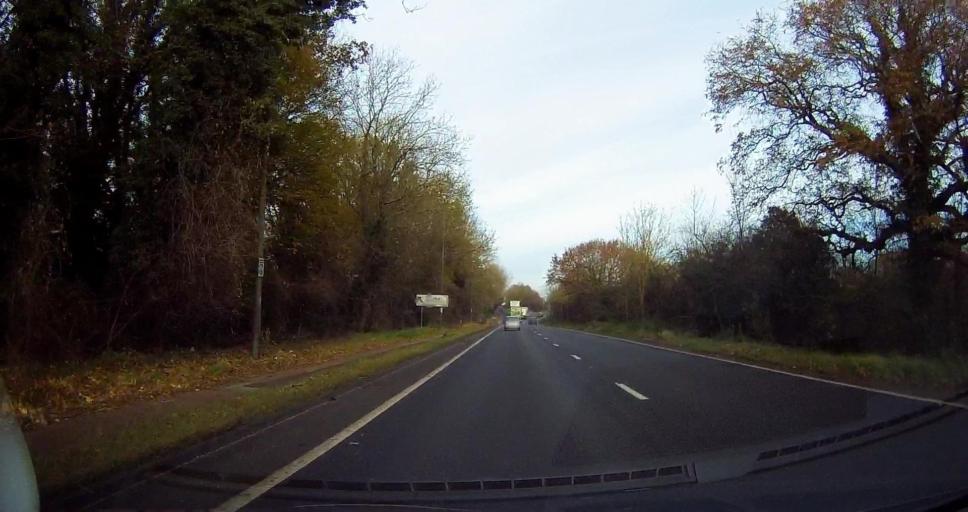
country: GB
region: England
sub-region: West Sussex
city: Hurstpierpoint
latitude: 50.9622
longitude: -0.1940
